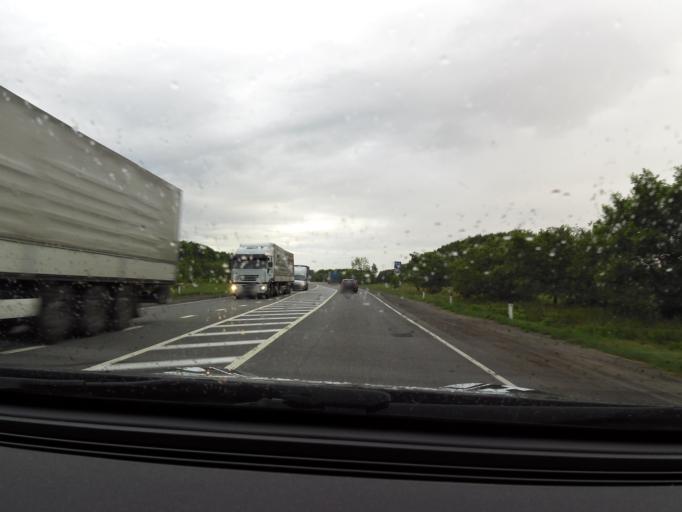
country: RU
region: Chuvashia
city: Yantikovo
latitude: 55.7990
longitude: 47.8504
